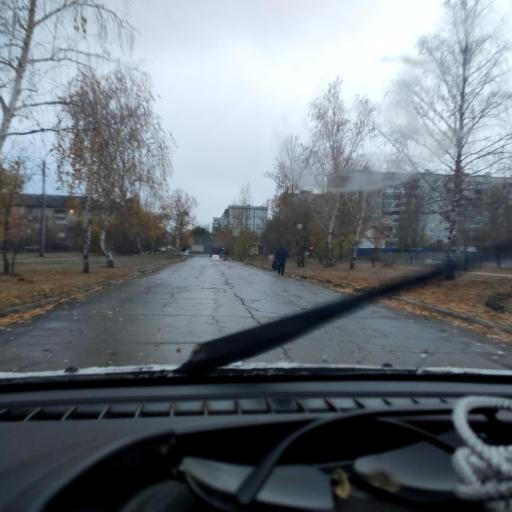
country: RU
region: Samara
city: Zhigulevsk
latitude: 53.4677
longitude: 49.5389
